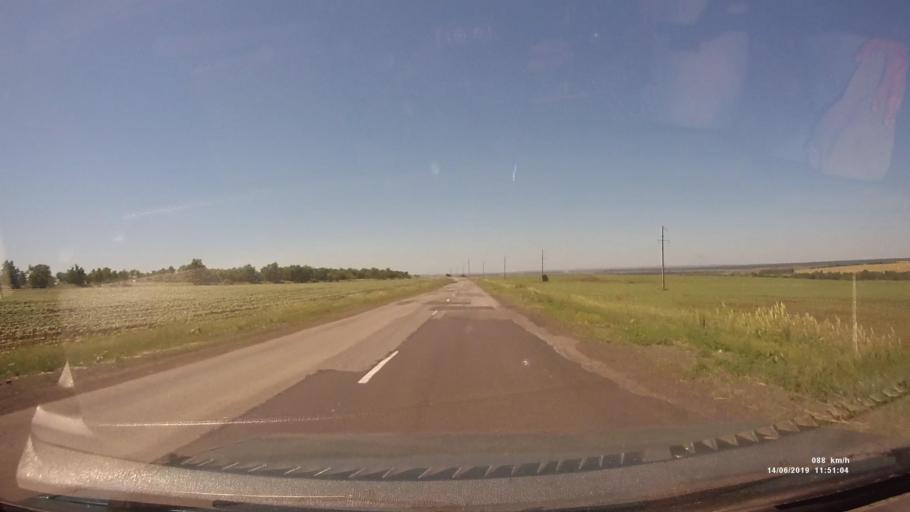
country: RU
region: Rostov
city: Kazanskaya
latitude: 49.8438
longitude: 41.2535
